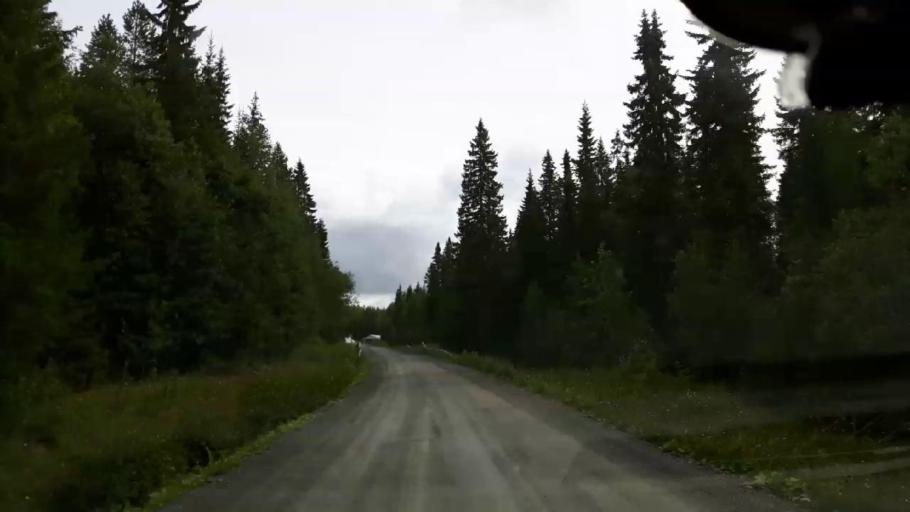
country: SE
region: Jaemtland
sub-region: Krokoms Kommun
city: Valla
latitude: 63.6379
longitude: 14.0102
